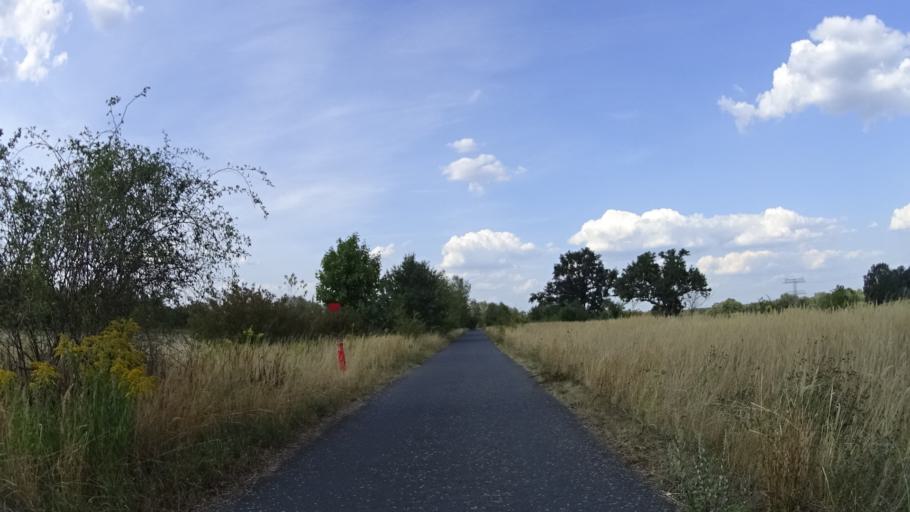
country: DE
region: Saxony
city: Ostritz
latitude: 51.0779
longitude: 14.9698
